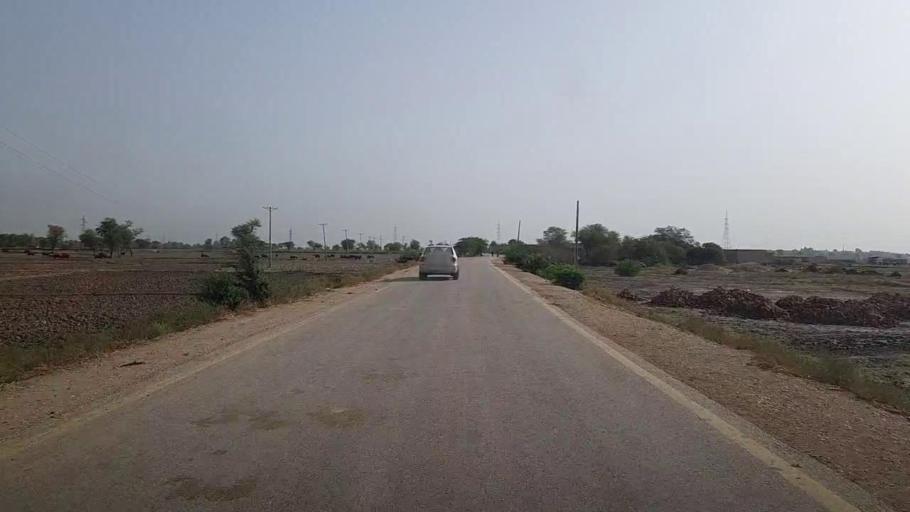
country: PK
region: Sindh
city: Khairpur Nathan Shah
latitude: 27.1007
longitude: 67.7557
